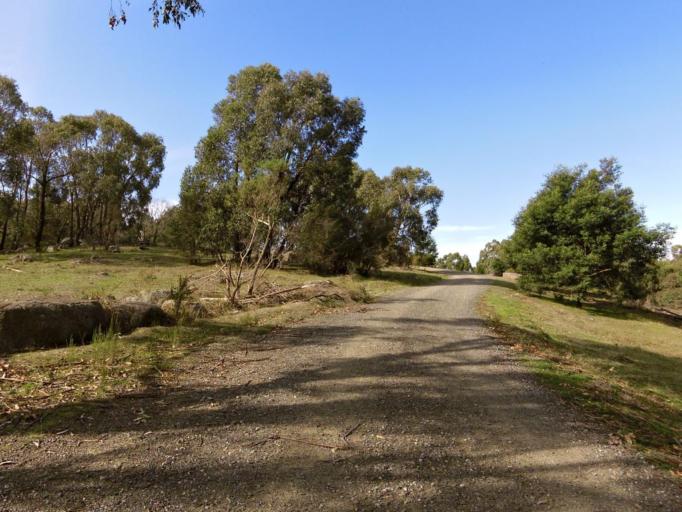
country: AU
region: Victoria
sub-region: Casey
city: Endeavour Hills
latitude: -37.9437
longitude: 145.2670
